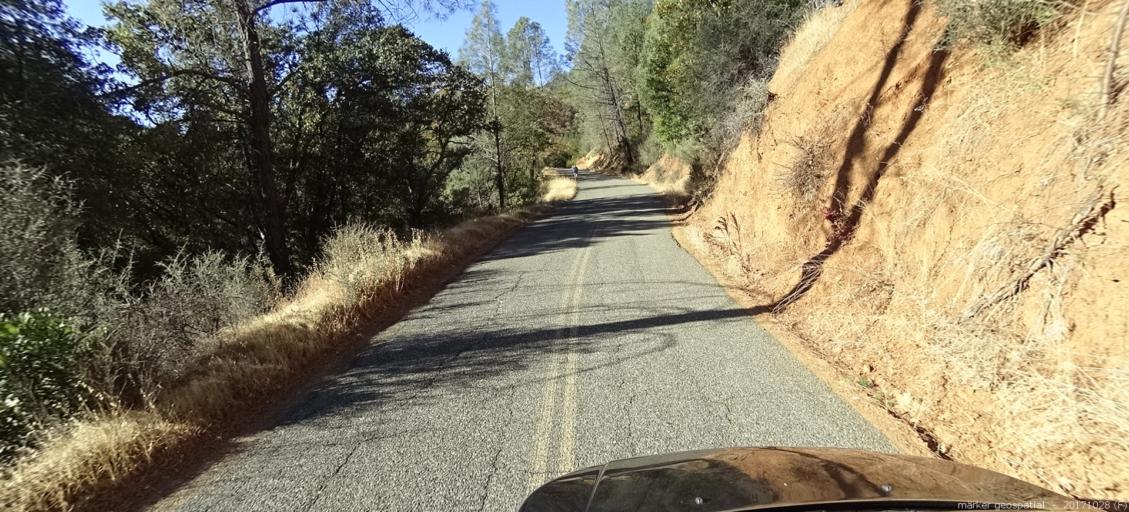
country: US
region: California
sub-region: Trinity County
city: Lewiston
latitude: 40.6655
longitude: -122.6545
